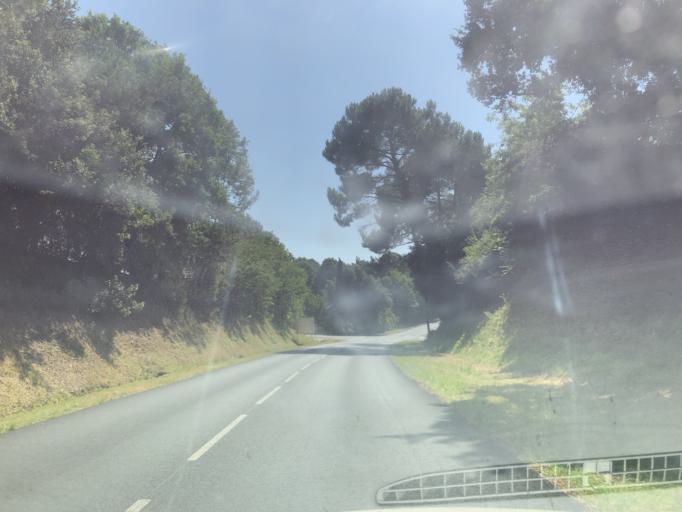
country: FR
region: Poitou-Charentes
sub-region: Departement de la Charente-Maritime
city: Meschers-sur-Gironde
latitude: 45.5642
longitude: -0.9649
